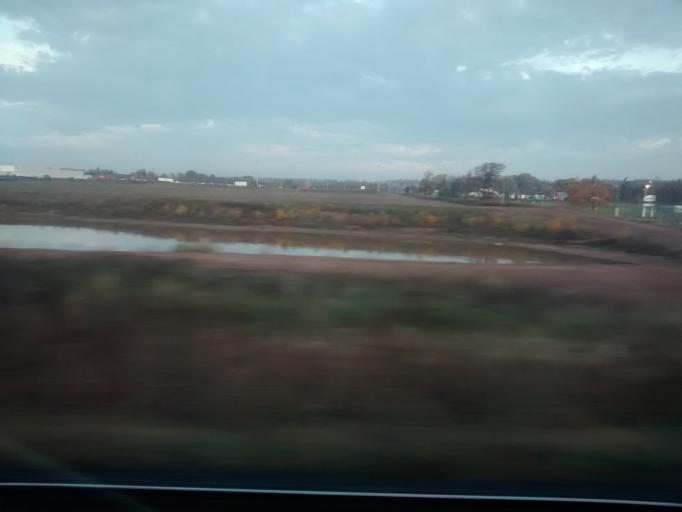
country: CA
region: Ontario
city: Oakville
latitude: 43.3987
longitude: -79.7411
